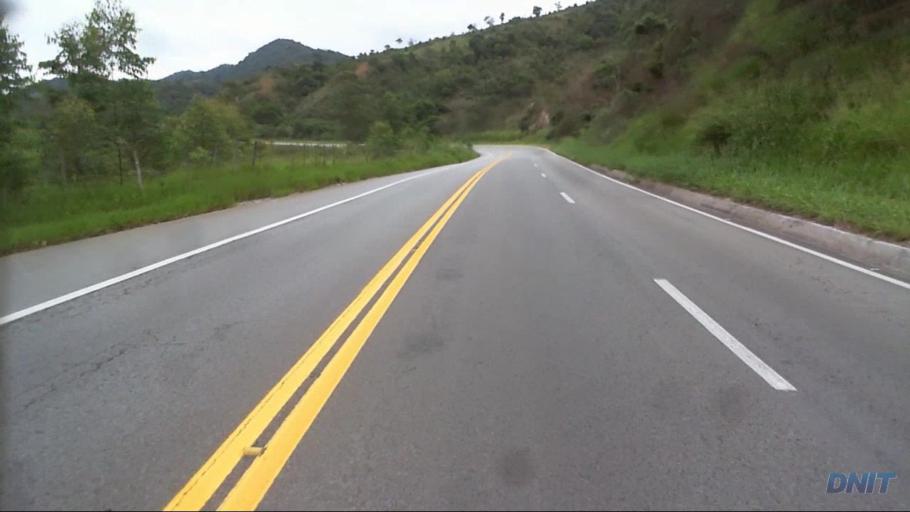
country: BR
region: Minas Gerais
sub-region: Nova Era
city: Nova Era
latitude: -19.6272
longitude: -42.8712
